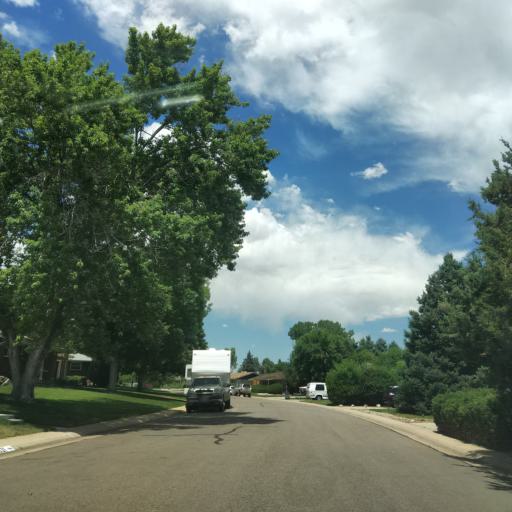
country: US
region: Colorado
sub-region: Jefferson County
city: Lakewood
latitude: 39.6838
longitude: -105.0932
